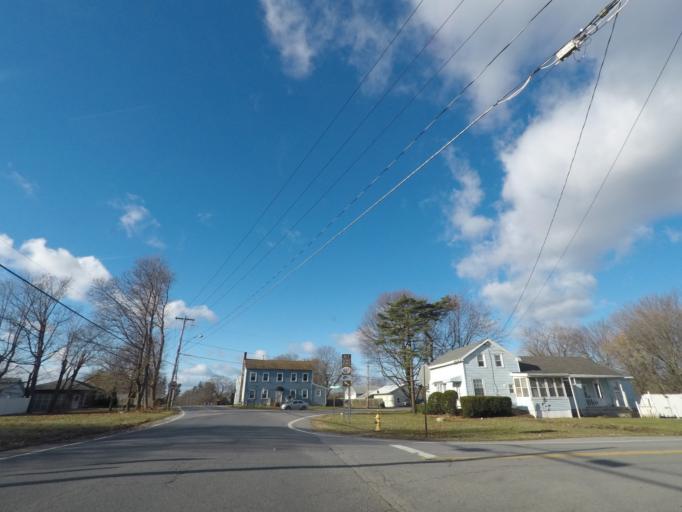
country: US
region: New York
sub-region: Saratoga County
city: Waterford
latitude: 42.8276
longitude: -73.7177
